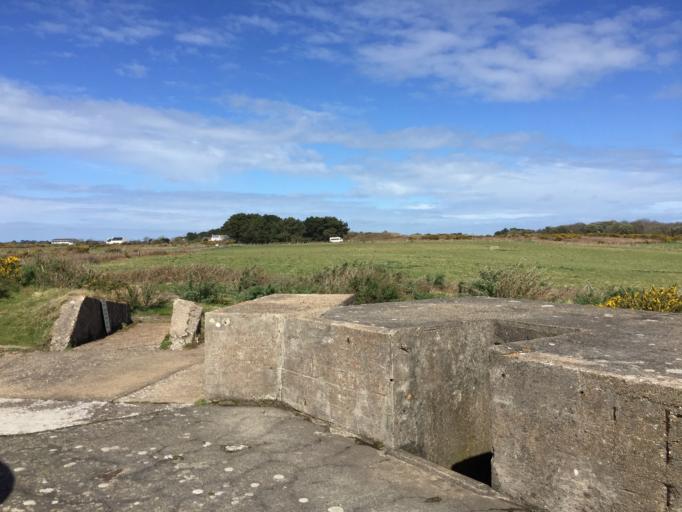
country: JE
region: St Helier
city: Saint Helier
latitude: 49.1688
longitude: -2.1684
